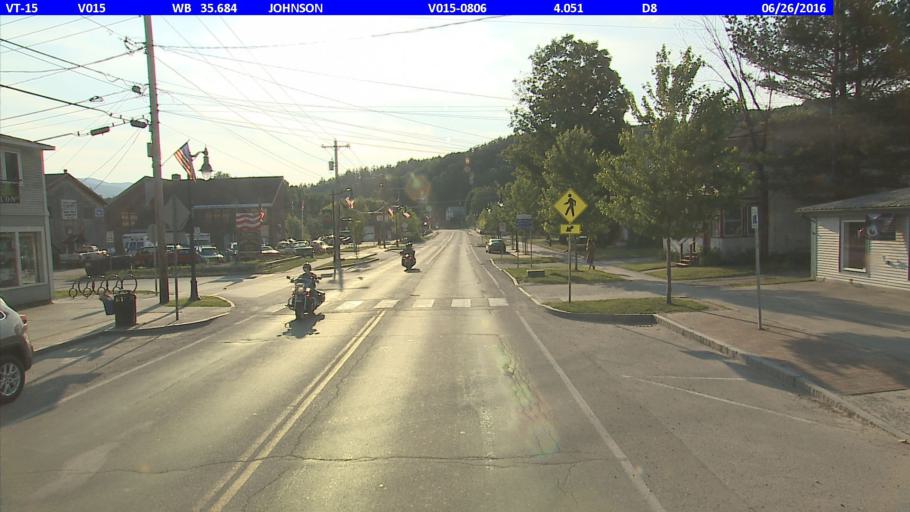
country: US
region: Vermont
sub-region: Lamoille County
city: Johnson
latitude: 44.6355
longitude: -72.6801
